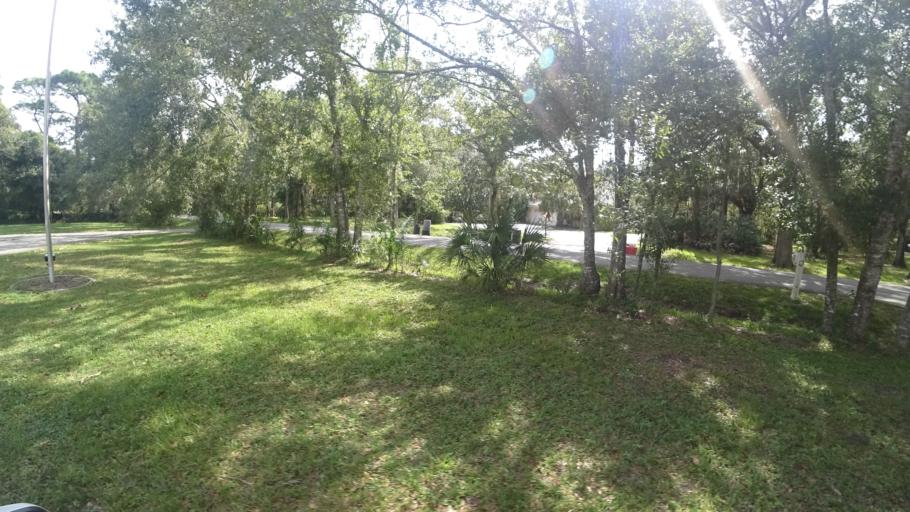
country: US
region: Florida
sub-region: Sarasota County
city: North Sarasota
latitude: 27.3871
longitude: -82.5094
